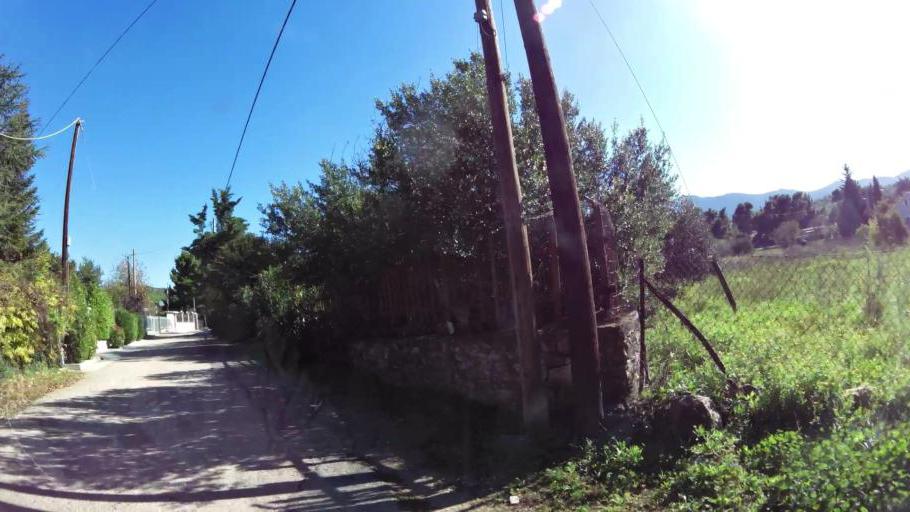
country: GR
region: Attica
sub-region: Nomarchia Anatolikis Attikis
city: Rodopoli
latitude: 38.1171
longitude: 23.8789
